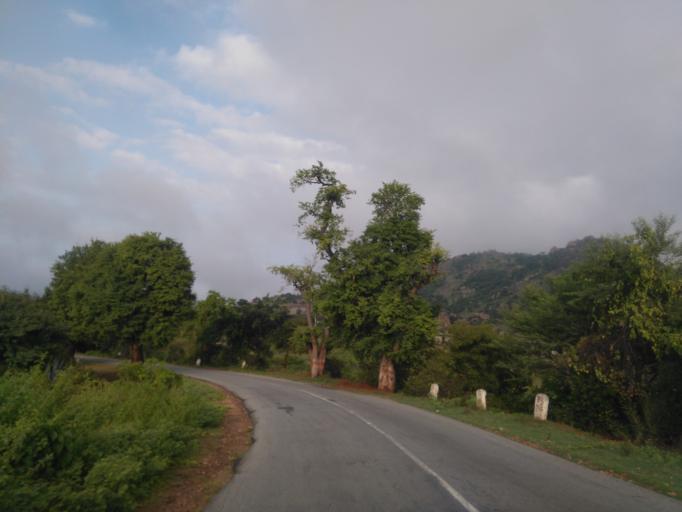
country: IN
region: Karnataka
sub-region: Ramanagara
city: Kanakapura
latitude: 12.4991
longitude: 77.3835
